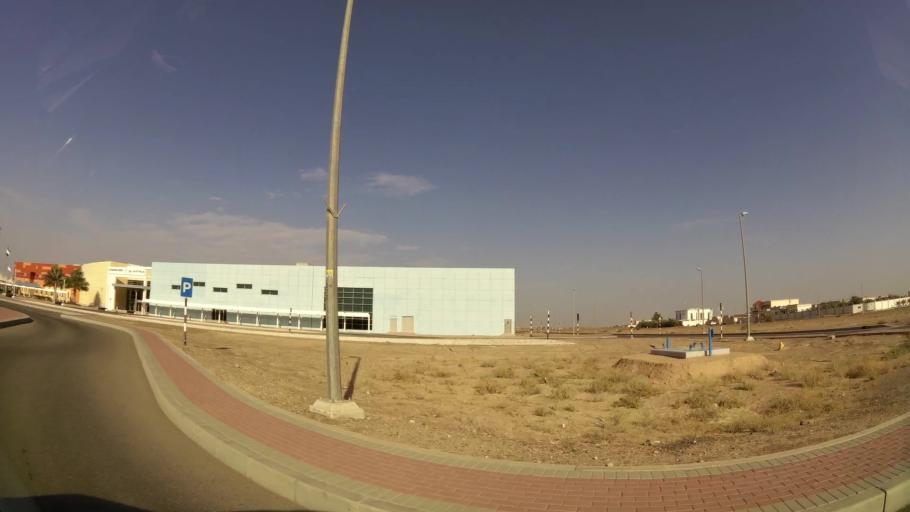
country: AE
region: Abu Dhabi
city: Al Ain
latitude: 24.0474
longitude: 55.8422
